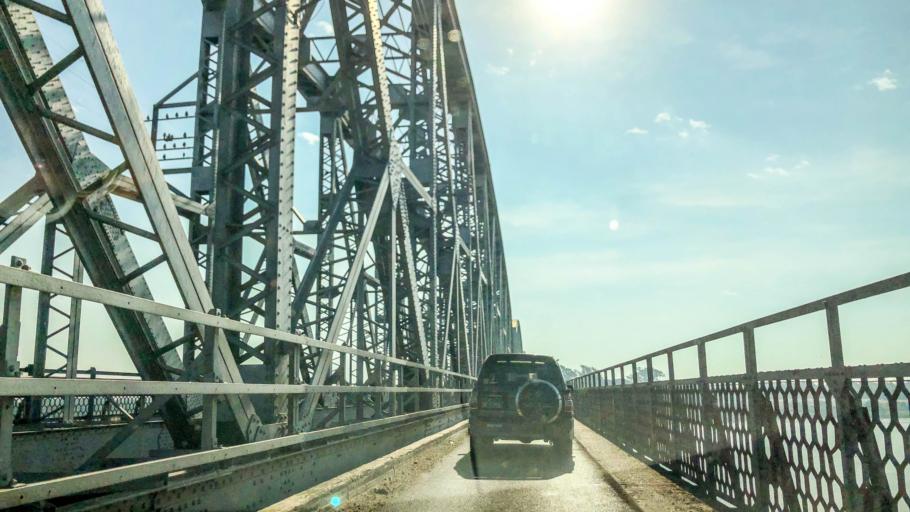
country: MM
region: Sagain
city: Sagaing
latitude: 21.8723
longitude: 95.9912
